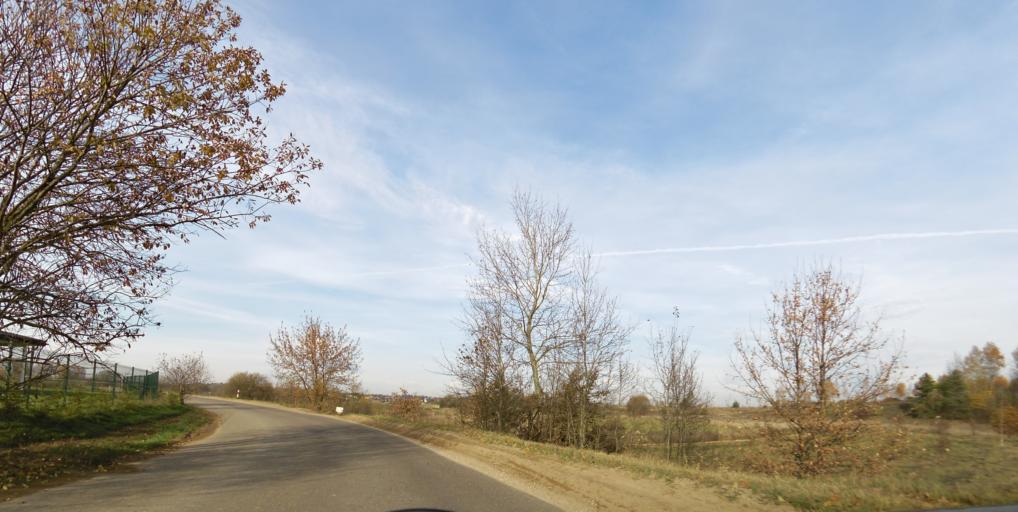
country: LT
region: Vilnius County
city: Pilaite
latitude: 54.7213
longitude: 25.1578
